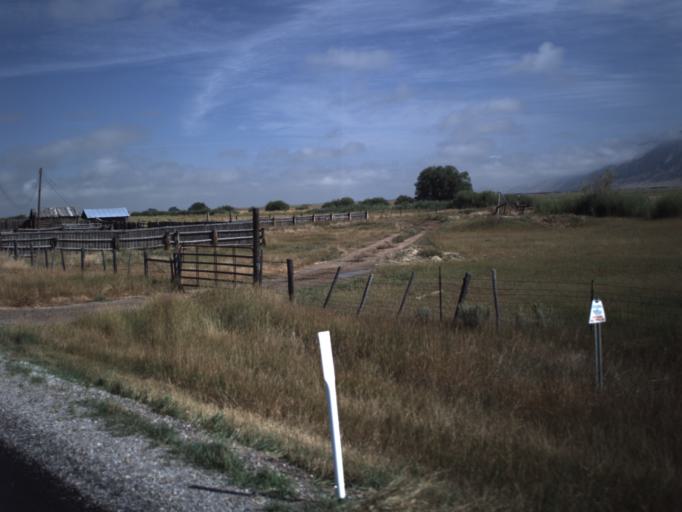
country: US
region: Utah
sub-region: Rich County
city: Randolph
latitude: 41.6108
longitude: -111.1790
